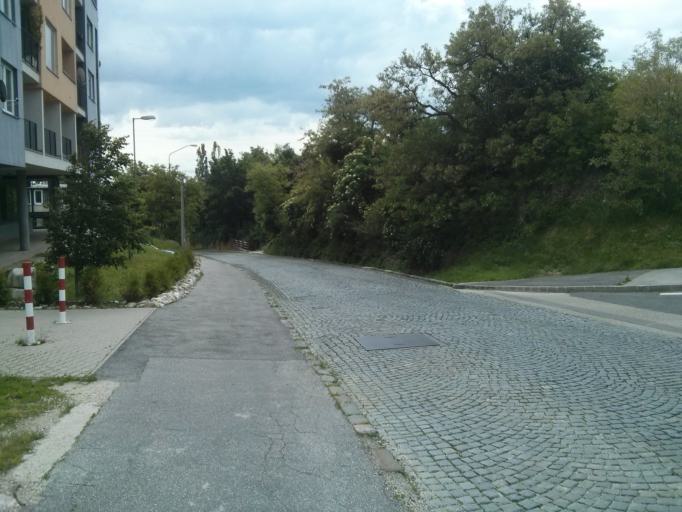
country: SK
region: Bratislavsky
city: Bratislava
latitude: 48.1732
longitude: 17.1217
